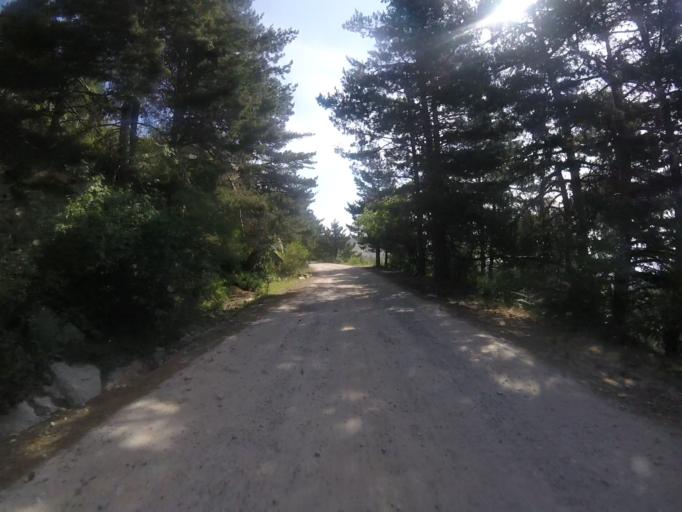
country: ES
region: Madrid
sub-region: Provincia de Madrid
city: Guadarrama
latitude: 40.6901
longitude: -4.1535
